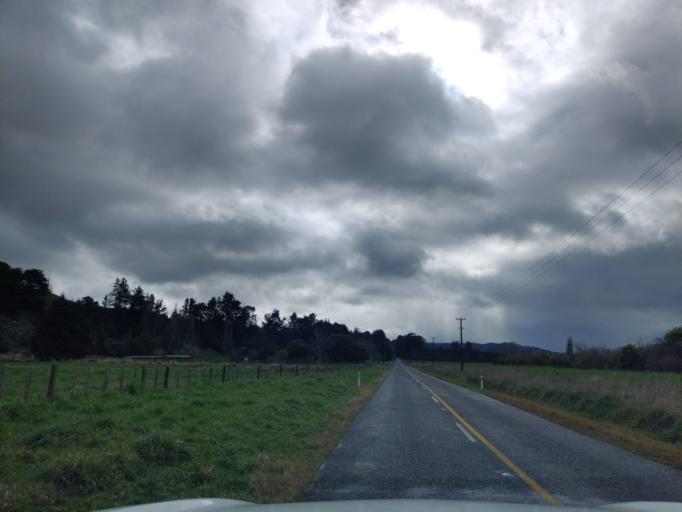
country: NZ
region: Manawatu-Wanganui
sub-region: Palmerston North City
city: Palmerston North
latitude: -40.2017
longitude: 175.7796
